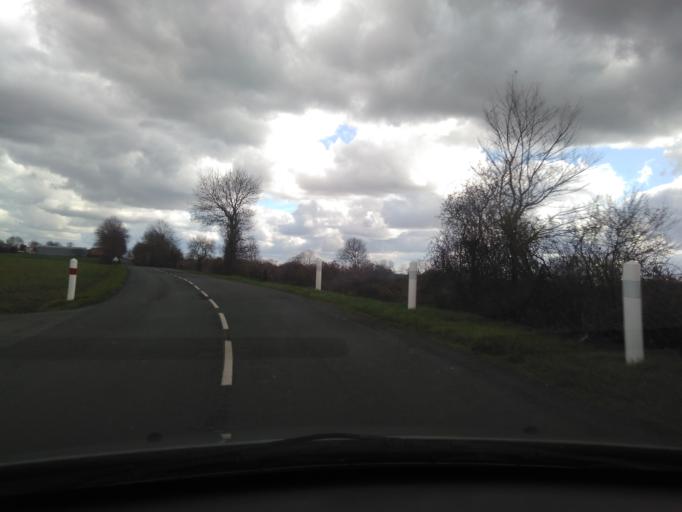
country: FR
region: Pays de la Loire
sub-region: Departement de la Vendee
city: Les Essarts
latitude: 46.7502
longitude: -1.2122
